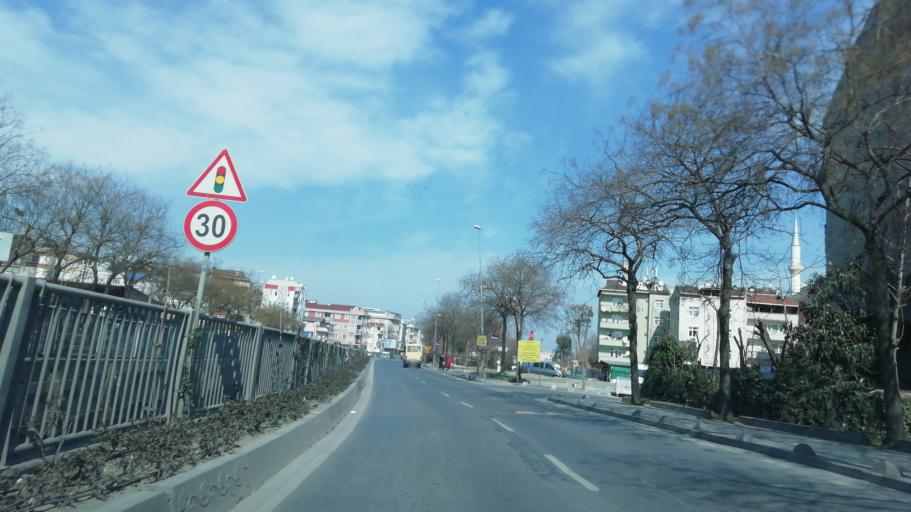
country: TR
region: Istanbul
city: Bagcilar
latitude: 41.0228
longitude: 28.8483
